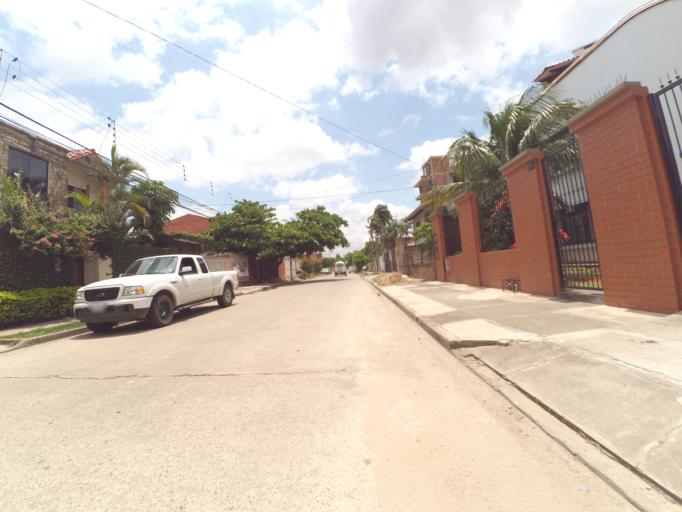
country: BO
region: Santa Cruz
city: Santa Cruz de la Sierra
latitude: -17.7868
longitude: -63.2032
